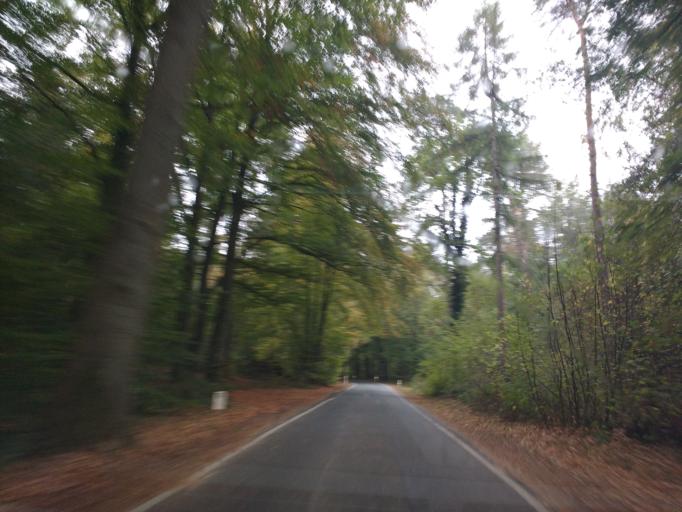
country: DE
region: North Rhine-Westphalia
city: Borgholzhausen
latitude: 52.0602
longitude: 8.2889
